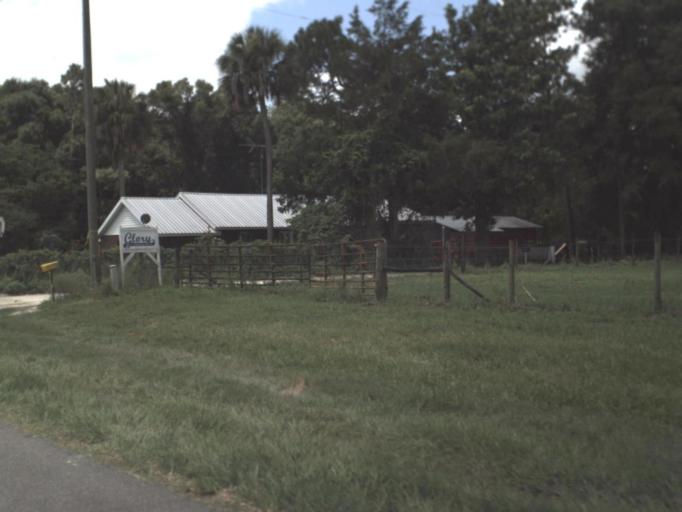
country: US
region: Florida
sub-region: Gilchrist County
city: Trenton
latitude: 29.7159
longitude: -82.8576
